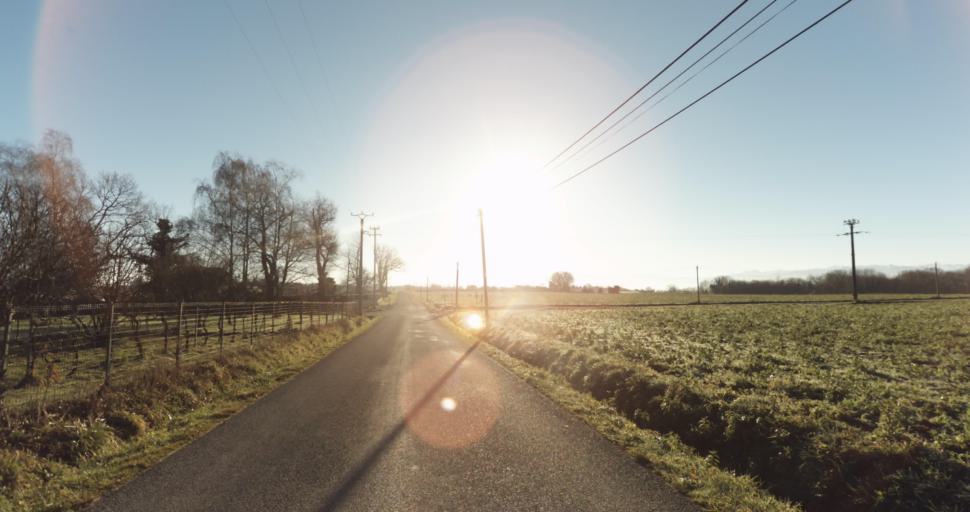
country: FR
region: Aquitaine
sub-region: Departement des Pyrenees-Atlantiques
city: Morlaas
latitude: 43.3215
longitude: -0.2504
